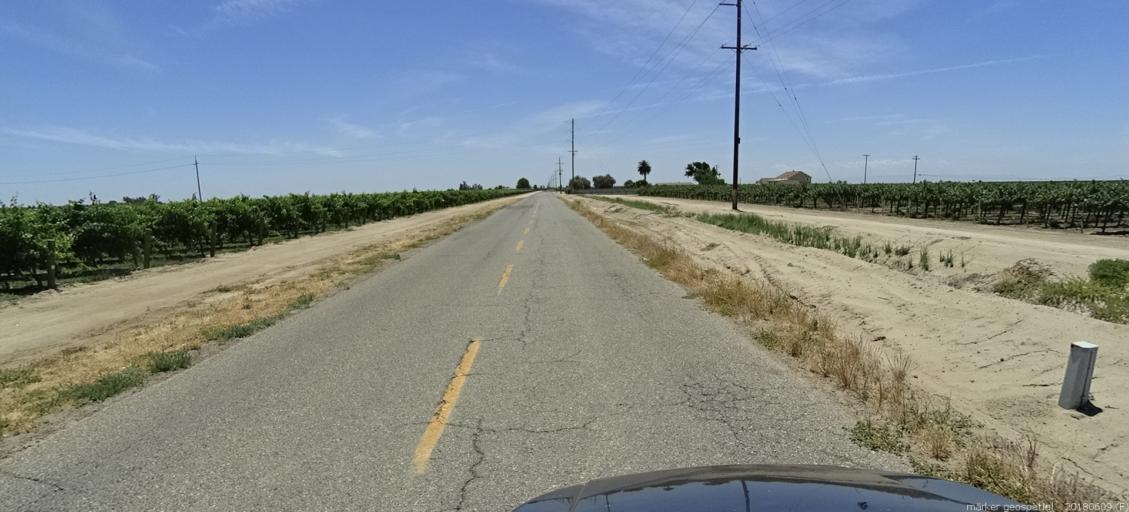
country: US
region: California
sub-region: Madera County
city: Madera
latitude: 36.9180
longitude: -120.1104
